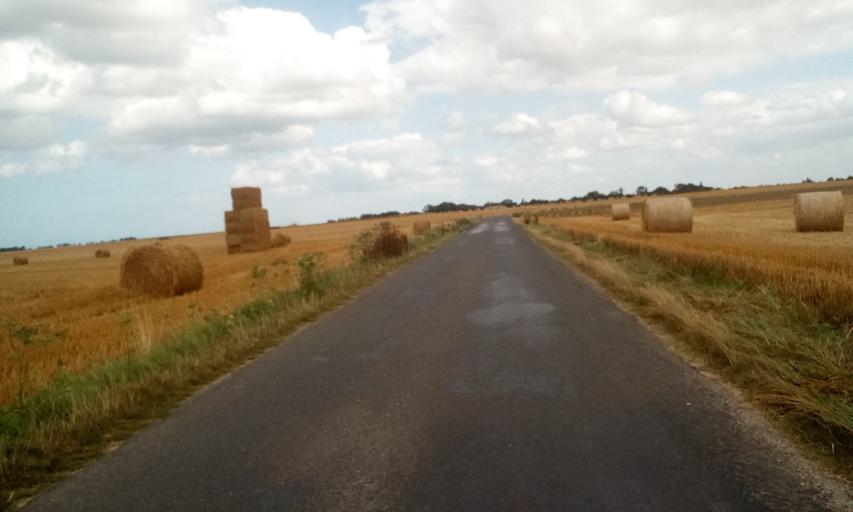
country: FR
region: Lower Normandy
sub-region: Departement du Calvados
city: Ver-sur-Mer
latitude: 49.3138
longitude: -0.5323
